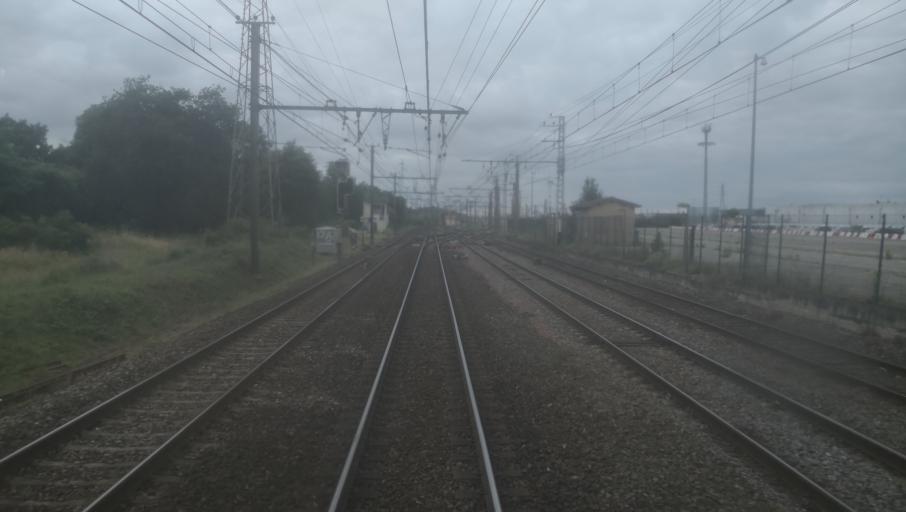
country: FR
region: Midi-Pyrenees
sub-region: Departement de la Haute-Garonne
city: Fenouillet
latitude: 43.6862
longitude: 1.4003
